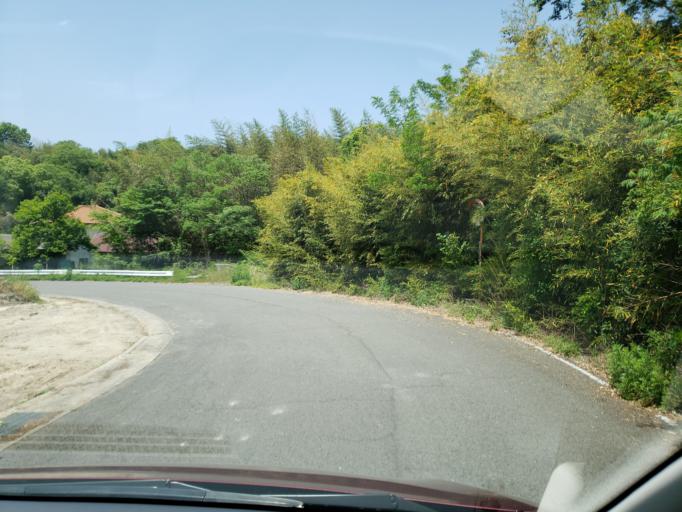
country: JP
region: Tokushima
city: Wakimachi
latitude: 34.0847
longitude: 134.2065
